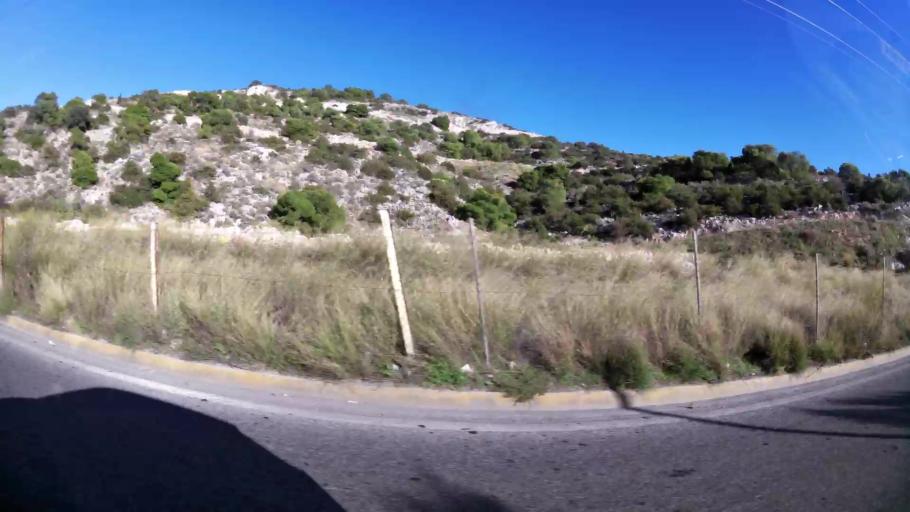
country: GR
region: Attica
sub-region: Nomarchia Athinas
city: Skaramangas
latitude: 37.9881
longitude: 23.5904
